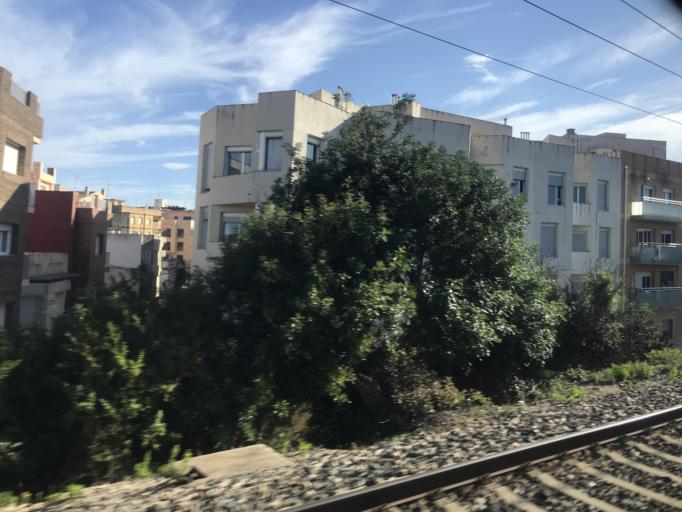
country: ES
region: Catalonia
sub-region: Provincia de Tarragona
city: L'Ampolla
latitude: 40.8137
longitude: 0.7113
